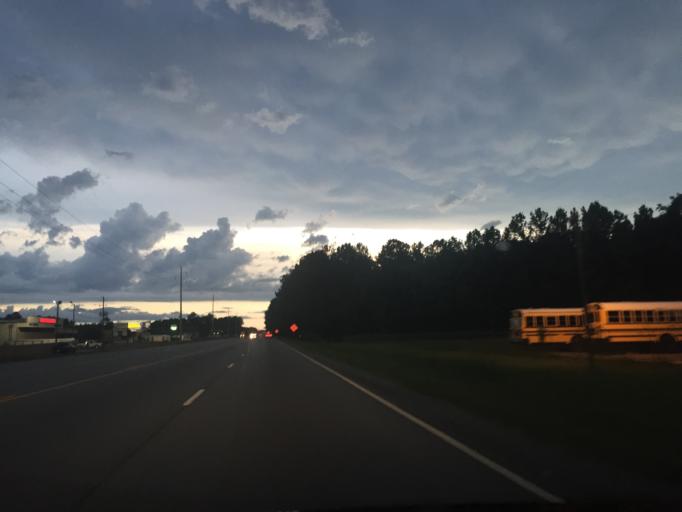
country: US
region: Georgia
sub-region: Liberty County
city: Hinesville
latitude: 31.8355
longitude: -81.5355
